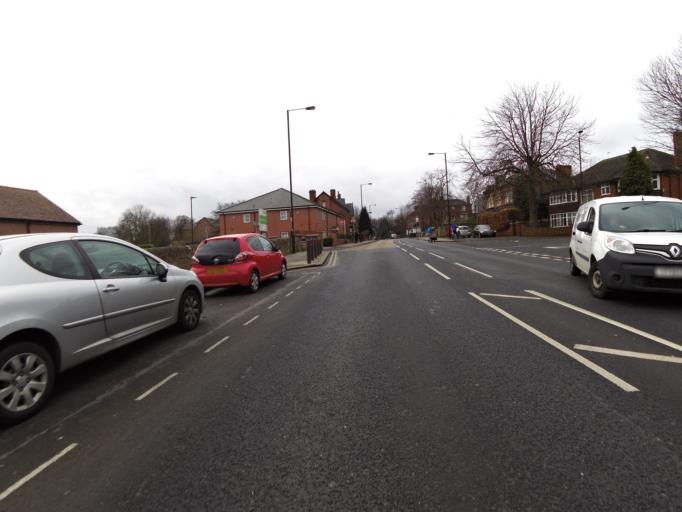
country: GB
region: England
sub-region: Doncaster
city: Doncaster
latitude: 53.5268
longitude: -1.1209
